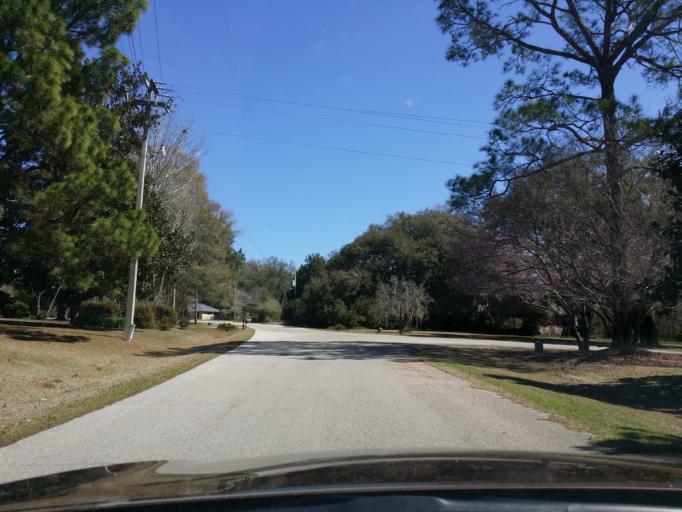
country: US
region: Florida
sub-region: Leon County
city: Tallahassee
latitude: 30.4790
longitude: -84.1844
